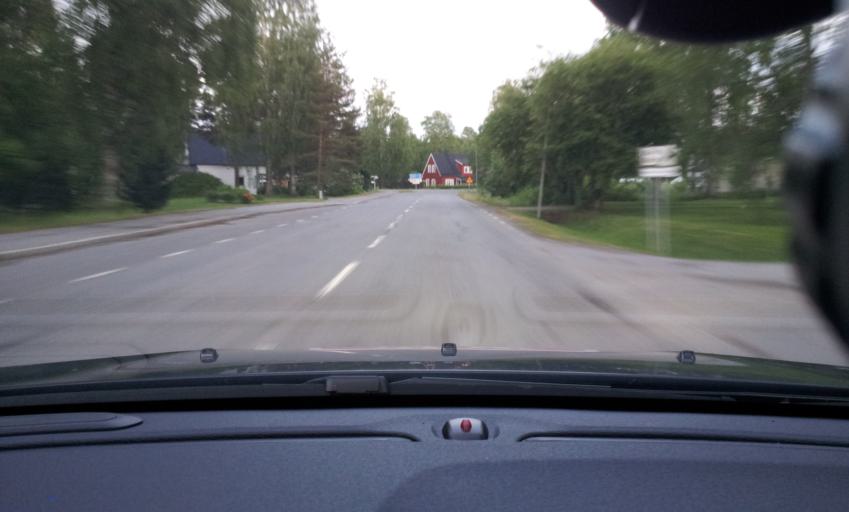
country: SE
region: Jaemtland
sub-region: Ragunda Kommun
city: Hammarstrand
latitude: 62.9827
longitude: 16.0883
